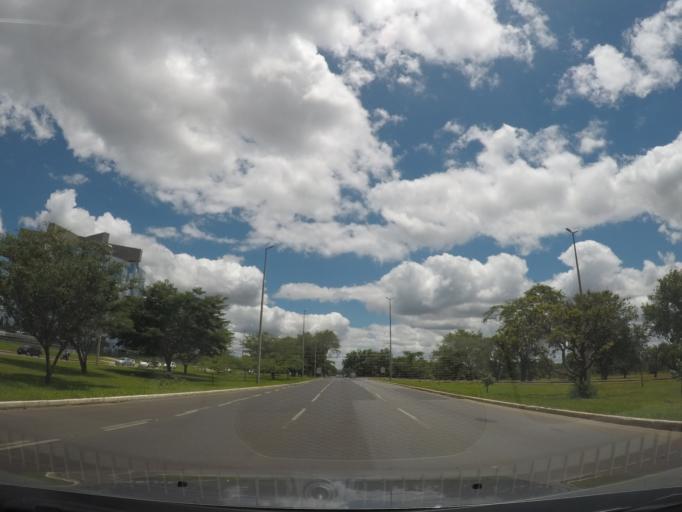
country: BR
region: Federal District
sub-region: Brasilia
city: Brasilia
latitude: -15.8092
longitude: -47.8598
